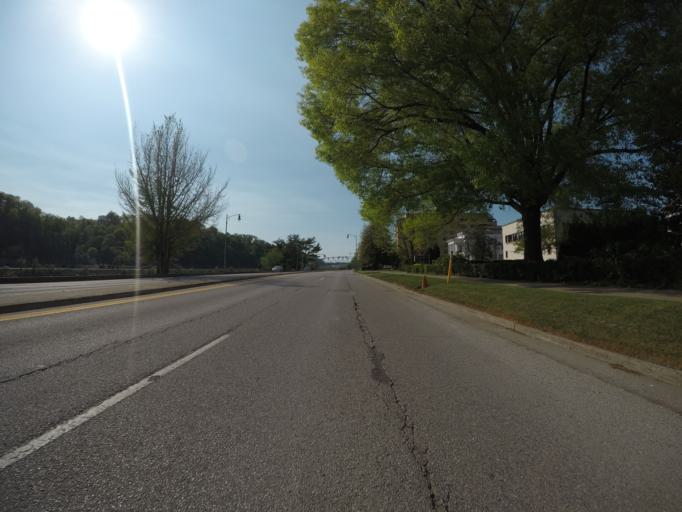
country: US
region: West Virginia
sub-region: Kanawha County
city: Charleston
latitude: 38.3426
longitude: -81.6300
